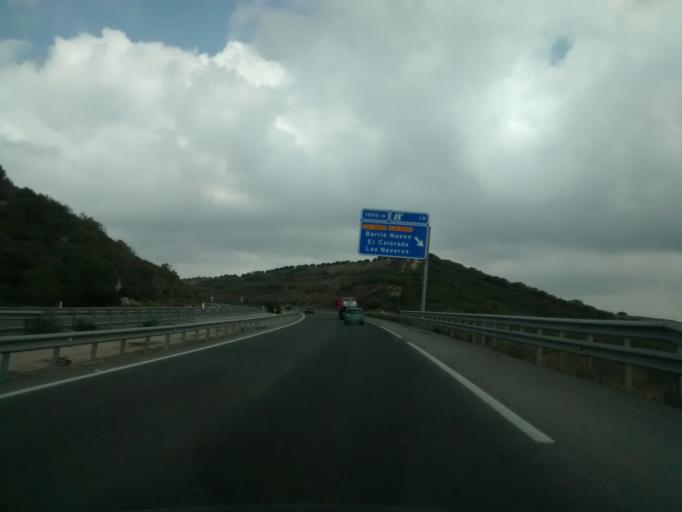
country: ES
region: Andalusia
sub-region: Provincia de Cadiz
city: Conil de la Frontera
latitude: 36.3392
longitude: -6.0490
